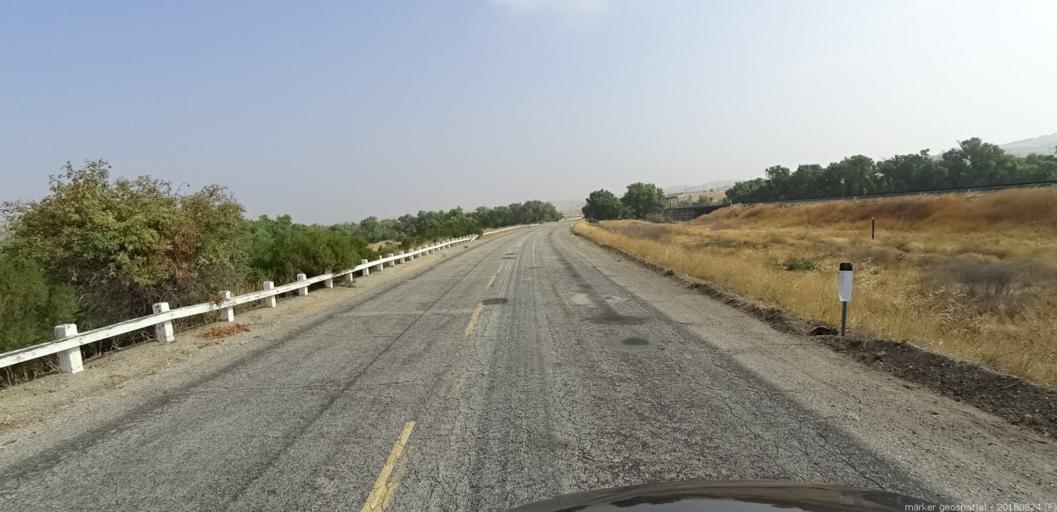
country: US
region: California
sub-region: San Luis Obispo County
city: San Miguel
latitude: 35.8212
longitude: -120.7537
